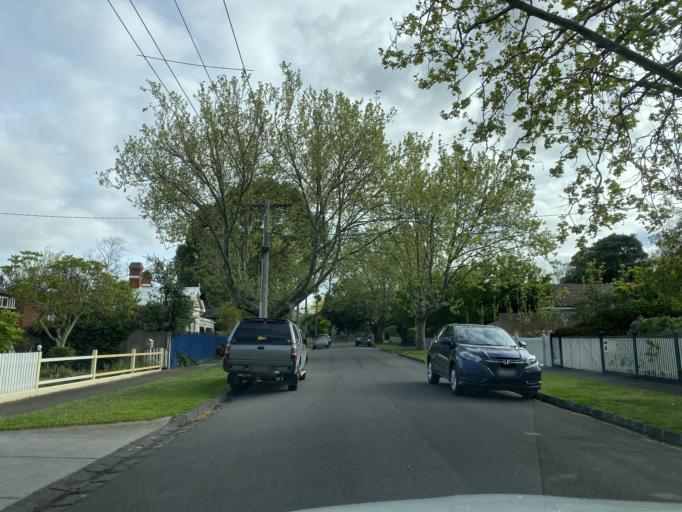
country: AU
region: Victoria
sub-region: Boroondara
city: Canterbury
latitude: -37.8335
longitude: 145.0864
